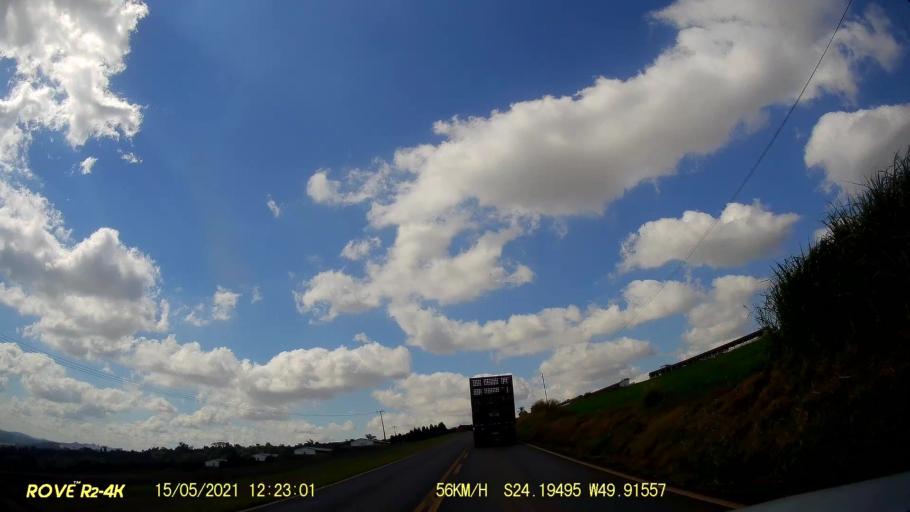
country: BR
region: Parana
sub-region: Jaguariaiva
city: Jaguariaiva
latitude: -24.1947
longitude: -49.9153
